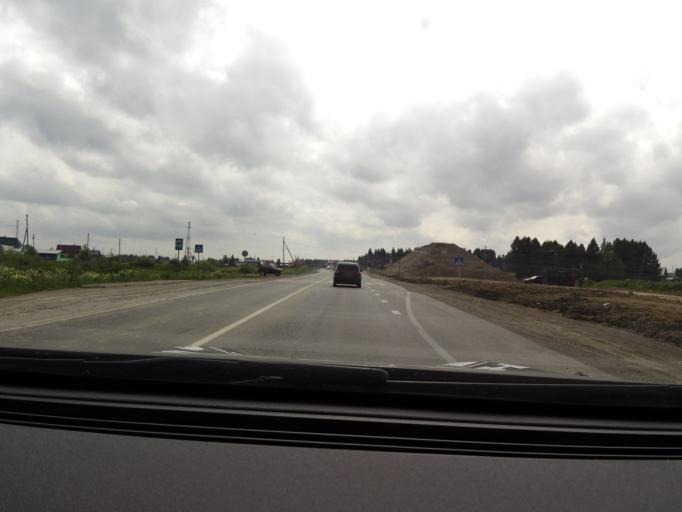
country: RU
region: Perm
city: Kukushtan
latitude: 57.6456
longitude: 56.4463
